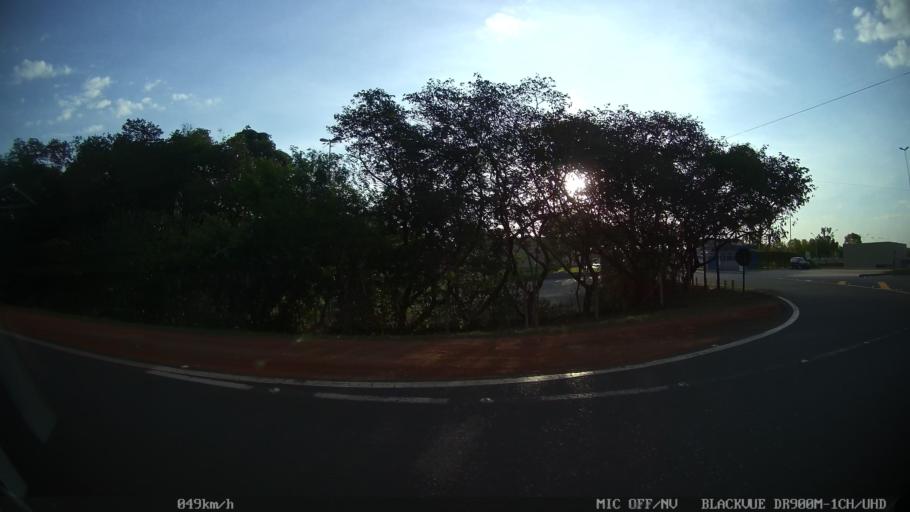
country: BR
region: Sao Paulo
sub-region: Ribeirao Preto
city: Ribeirao Preto
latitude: -21.1058
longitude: -47.8109
